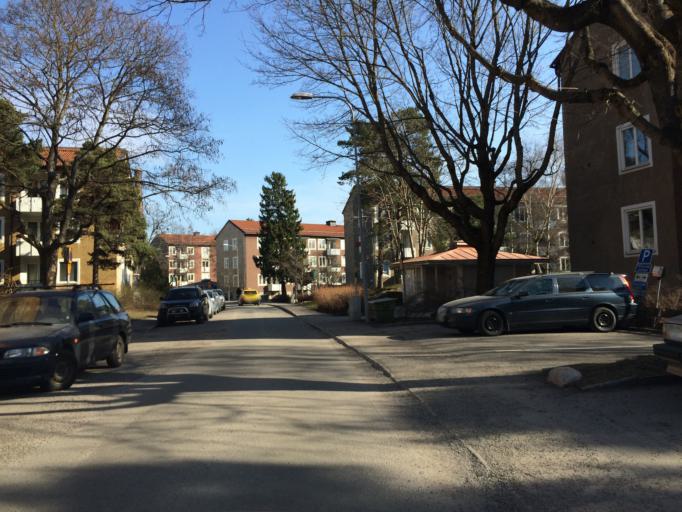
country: SE
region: Stockholm
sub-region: Stockholms Kommun
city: Arsta
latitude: 59.2880
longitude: 18.0001
